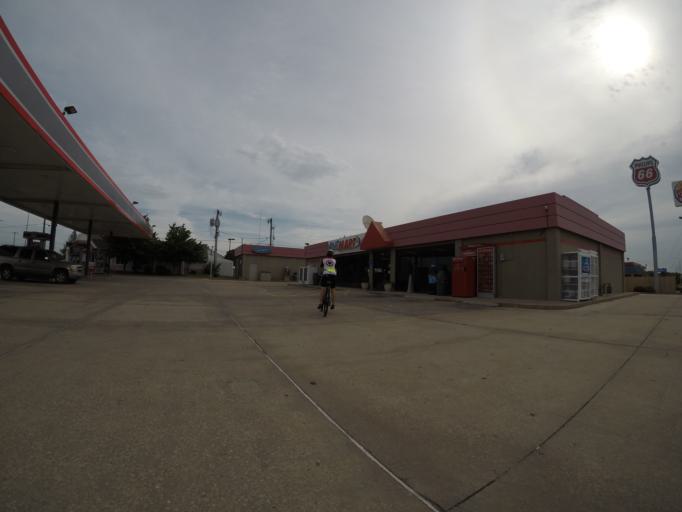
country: US
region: Kansas
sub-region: Franklin County
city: Ottawa
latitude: 38.5795
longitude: -95.2672
